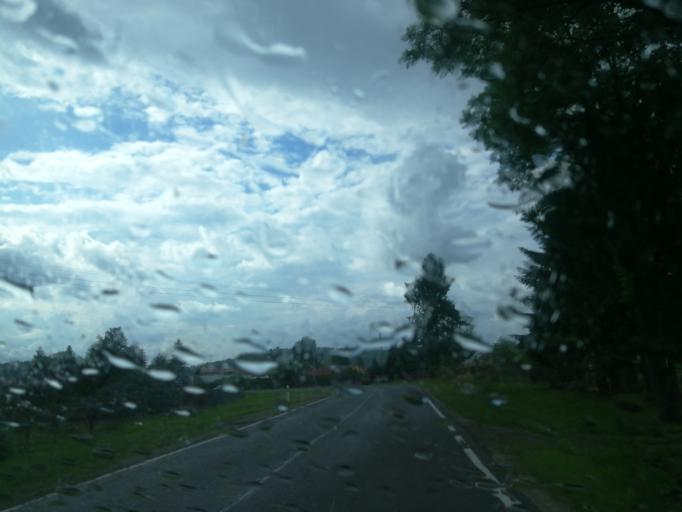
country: PL
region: Subcarpathian Voivodeship
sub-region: Powiat leski
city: Uherce Mineralne
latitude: 49.4587
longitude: 22.4094
